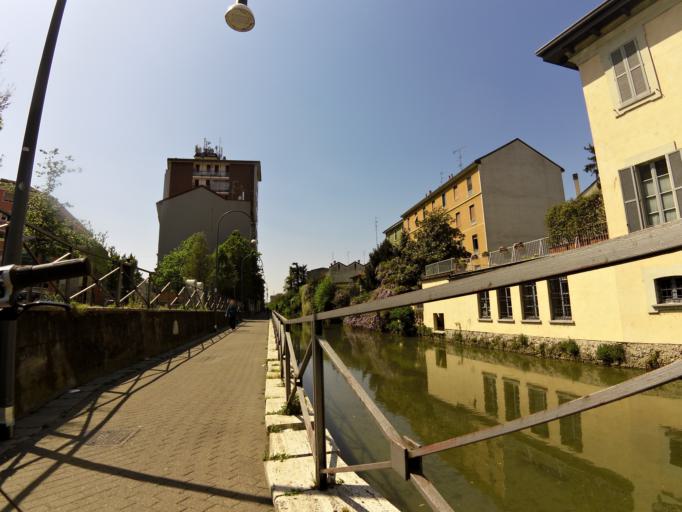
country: IT
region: Lombardy
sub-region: Citta metropolitana di Milano
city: Sesto San Giovanni
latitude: 45.5094
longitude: 9.2472
